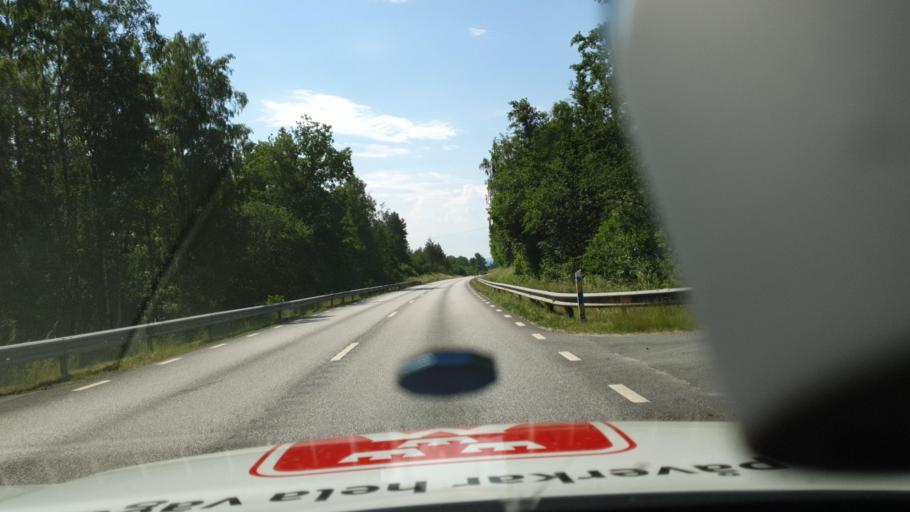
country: SE
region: Joenkoeping
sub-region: Habo Kommun
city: Habo
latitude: 58.0676
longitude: 14.1959
